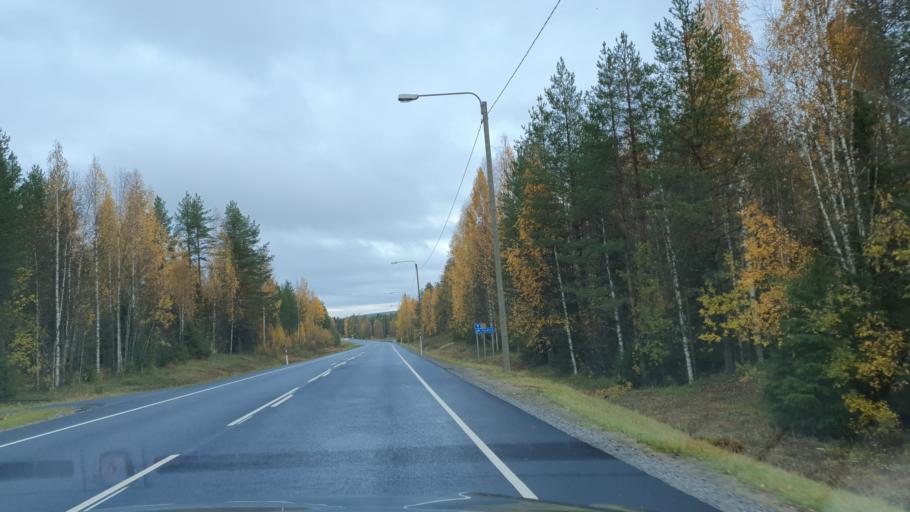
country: FI
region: Lapland
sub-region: Rovaniemi
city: Rovaniemi
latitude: 66.5414
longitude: 25.6587
